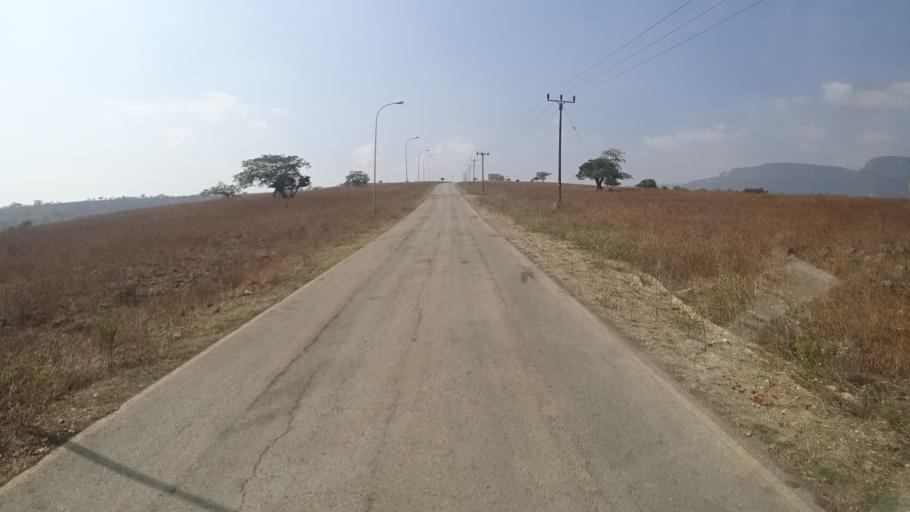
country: YE
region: Al Mahrah
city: Hawf
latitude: 16.7299
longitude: 53.2715
